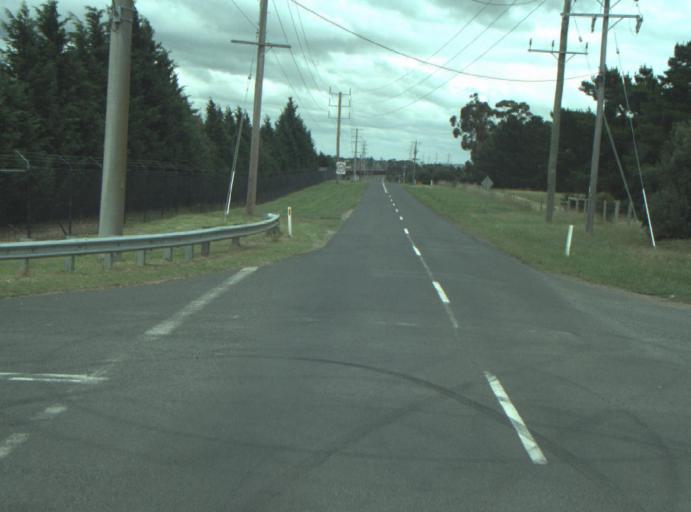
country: AU
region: Victoria
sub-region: Greater Geelong
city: Bell Post Hill
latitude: -38.0803
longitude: 144.3269
